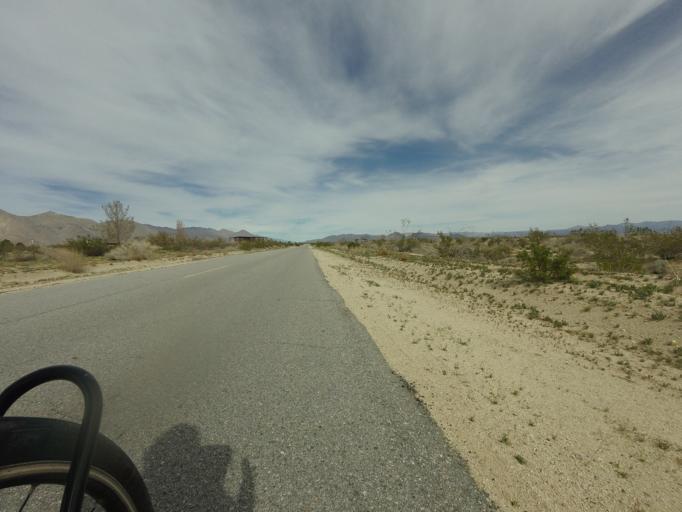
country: US
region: California
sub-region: Kern County
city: Inyokern
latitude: 35.7638
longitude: -117.8470
